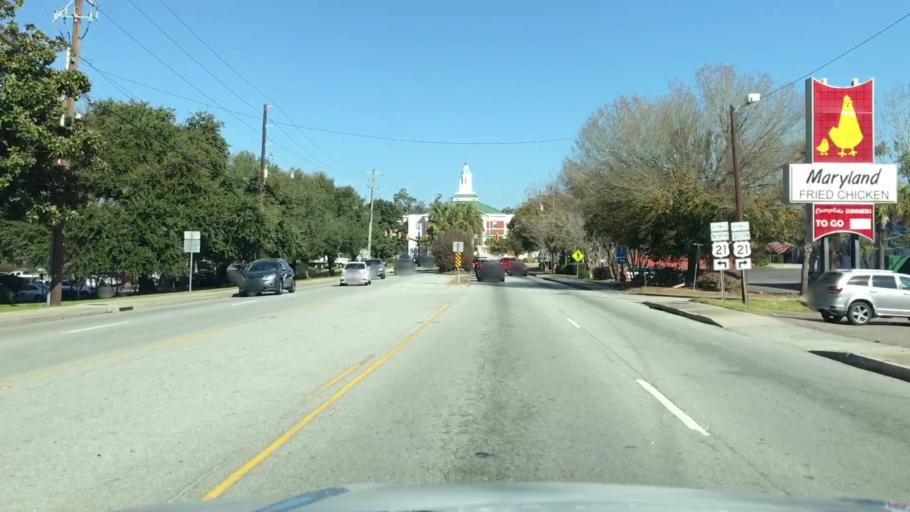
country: US
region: South Carolina
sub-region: Beaufort County
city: Beaufort
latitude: 32.4387
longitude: -80.6858
